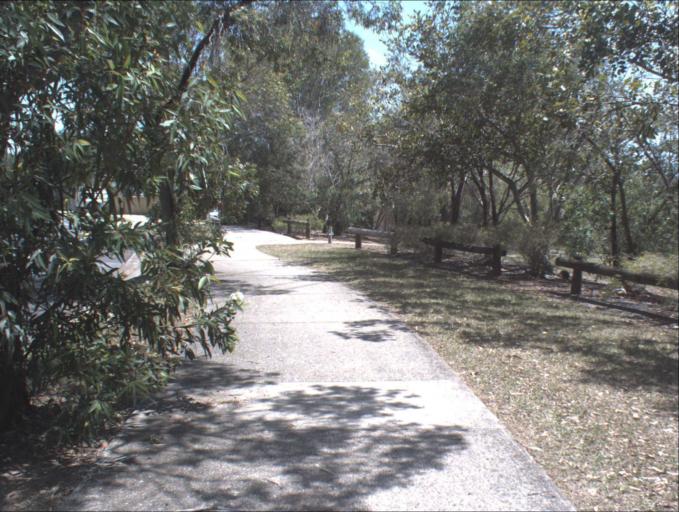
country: AU
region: Queensland
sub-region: Logan
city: Springwood
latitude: -27.6022
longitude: 153.1447
